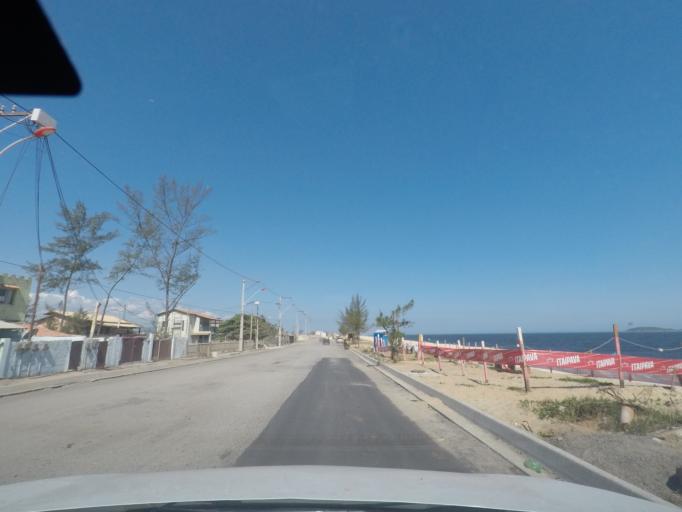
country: BR
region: Rio de Janeiro
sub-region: Marica
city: Marica
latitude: -22.9705
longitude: -42.9538
